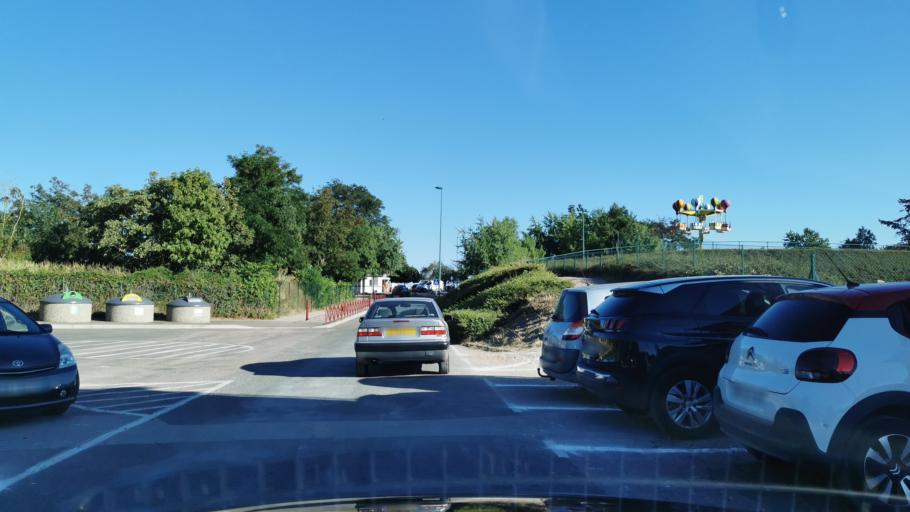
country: FR
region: Bourgogne
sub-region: Departement de Saone-et-Loire
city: Le Creusot
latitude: 46.8128
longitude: 4.4133
